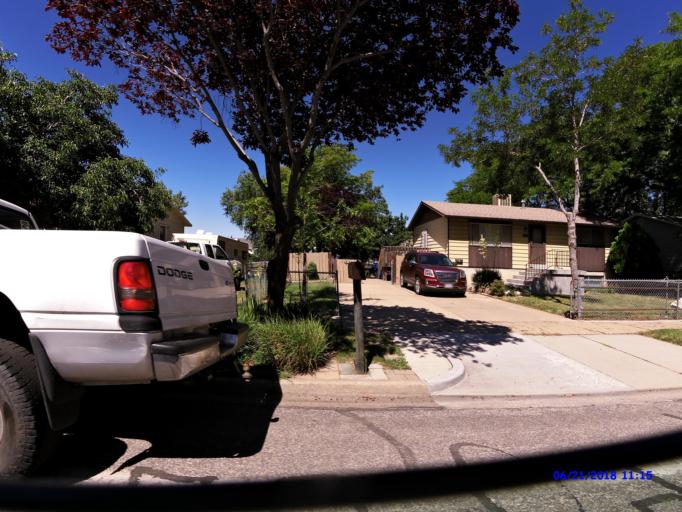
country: US
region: Utah
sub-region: Weber County
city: Harrisville
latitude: 41.2678
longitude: -111.9593
